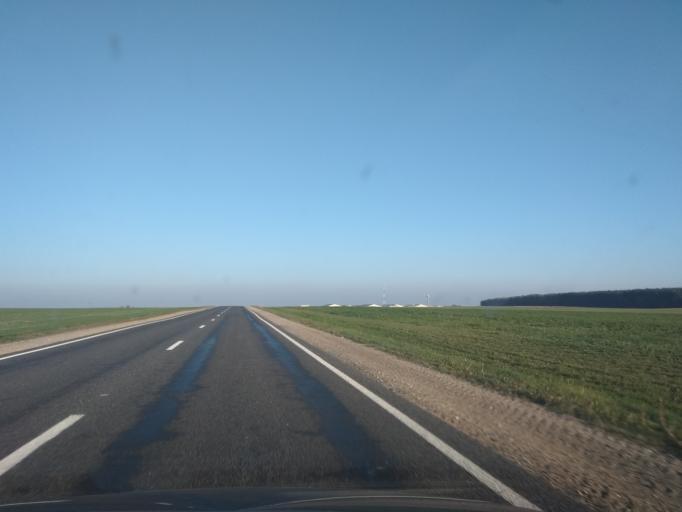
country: BY
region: Grodnenskaya
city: Svislach
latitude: 53.1298
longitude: 24.1618
